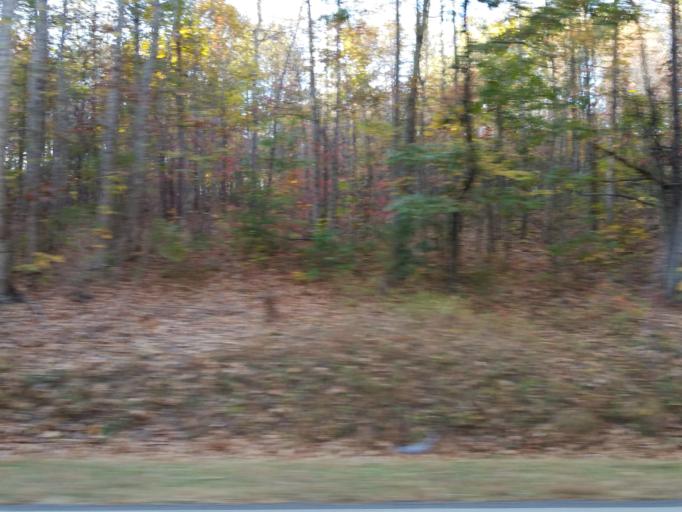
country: US
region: Georgia
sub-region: Pickens County
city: Jasper
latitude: 34.5666
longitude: -84.4731
